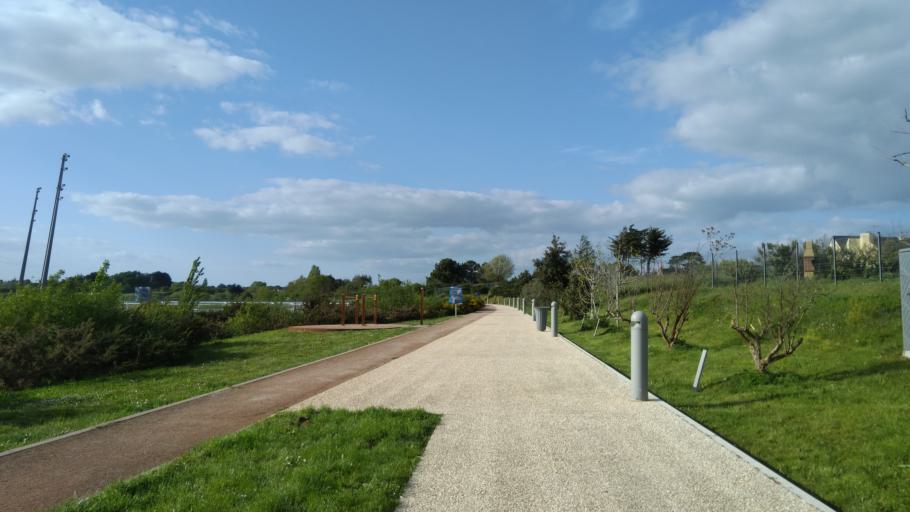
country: FR
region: Pays de la Loire
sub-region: Departement de la Loire-Atlantique
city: Pornichet
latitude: 47.2601
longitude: -2.3266
